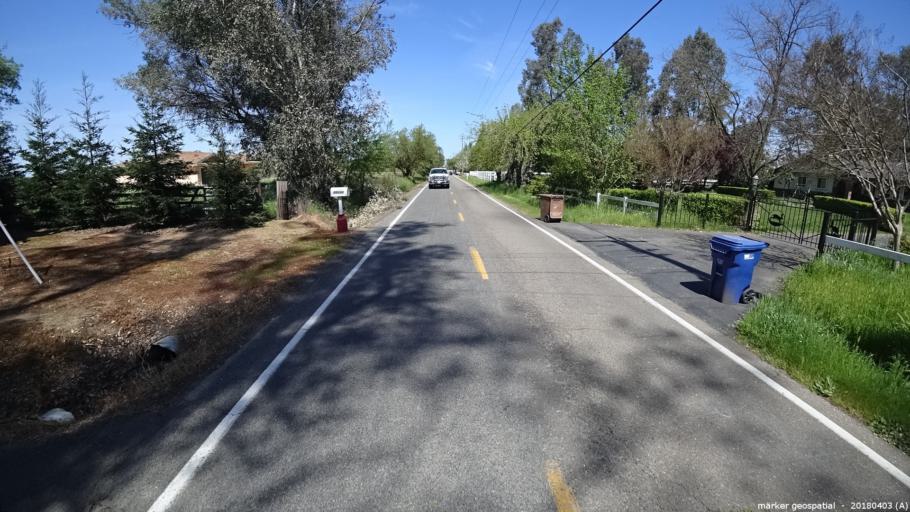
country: US
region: California
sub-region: Sacramento County
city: Wilton
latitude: 38.3851
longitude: -121.2607
